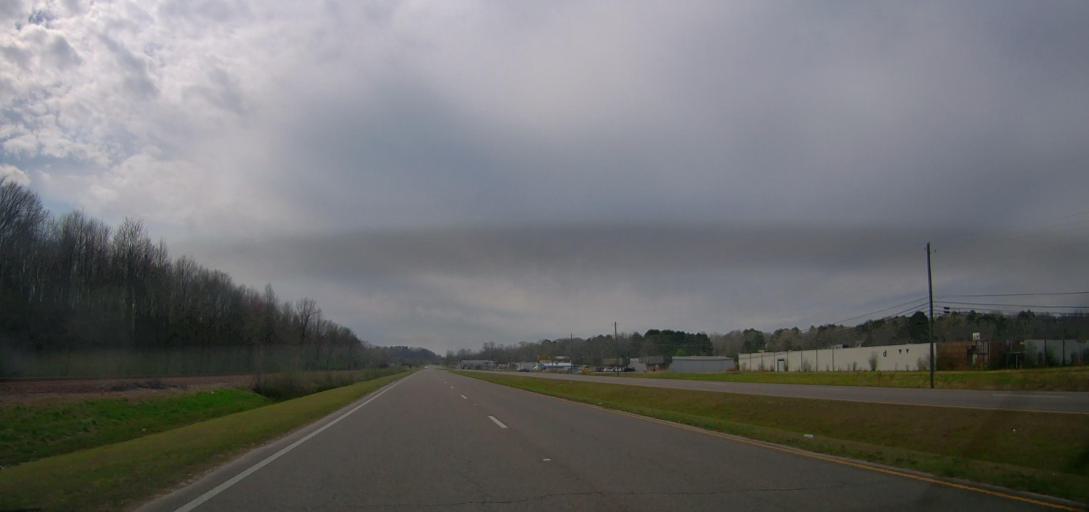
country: US
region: Alabama
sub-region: Walker County
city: Carbon Hill
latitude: 33.8845
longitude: -87.5178
